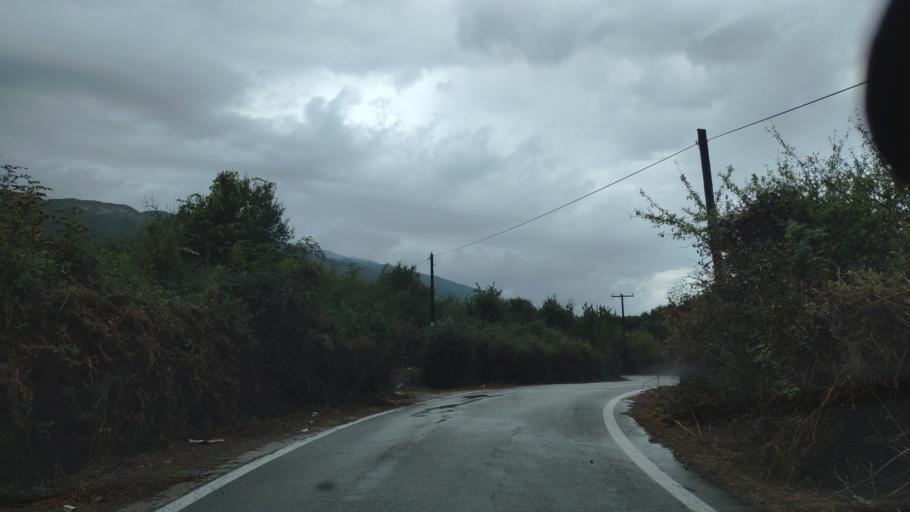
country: GR
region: Central Greece
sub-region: Nomos Evrytanias
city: Kerasochori
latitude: 39.1036
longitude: 21.4263
